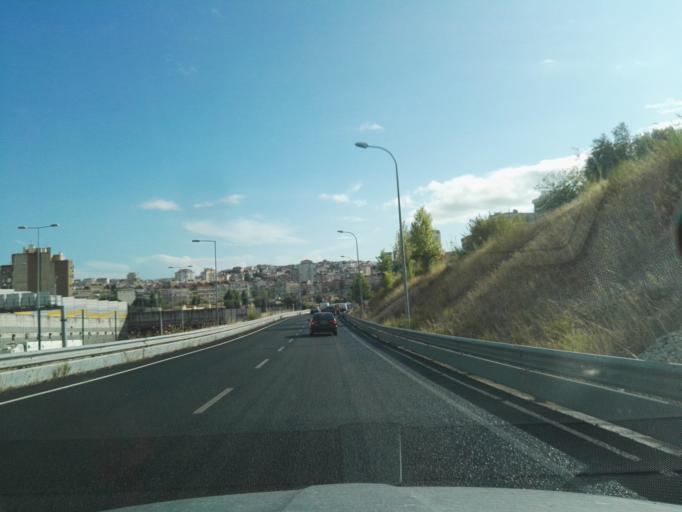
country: PT
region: Lisbon
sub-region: Odivelas
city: Pontinha
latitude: 38.7550
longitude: -9.2085
